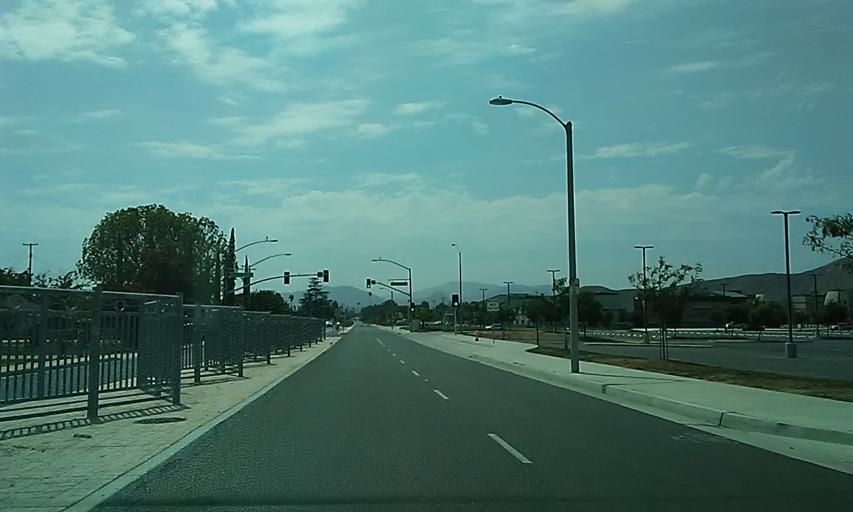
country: US
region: California
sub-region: Riverside County
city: Highgrove
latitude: 34.0194
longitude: -117.3248
